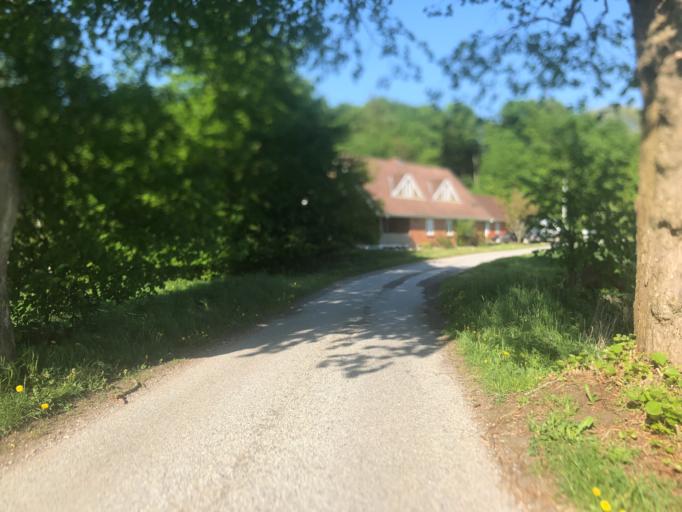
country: DK
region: Zealand
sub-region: Ringsted Kommune
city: Ringsted
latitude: 55.4812
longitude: 11.7882
